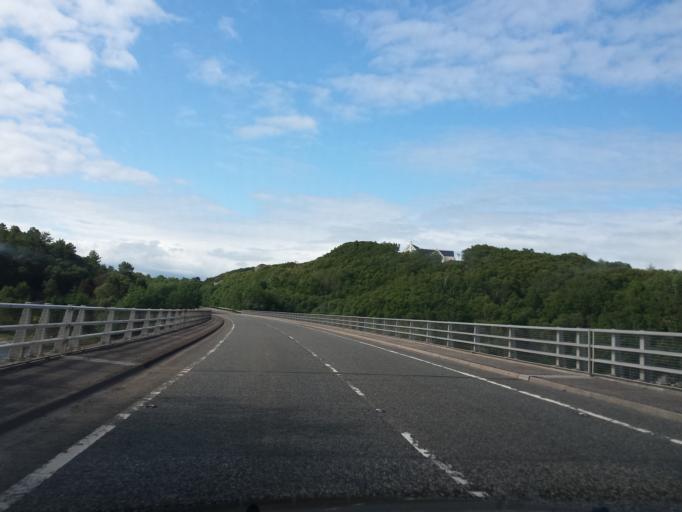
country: GB
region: Scotland
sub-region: Argyll and Bute
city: Isle Of Mull
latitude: 56.9615
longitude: -5.8189
